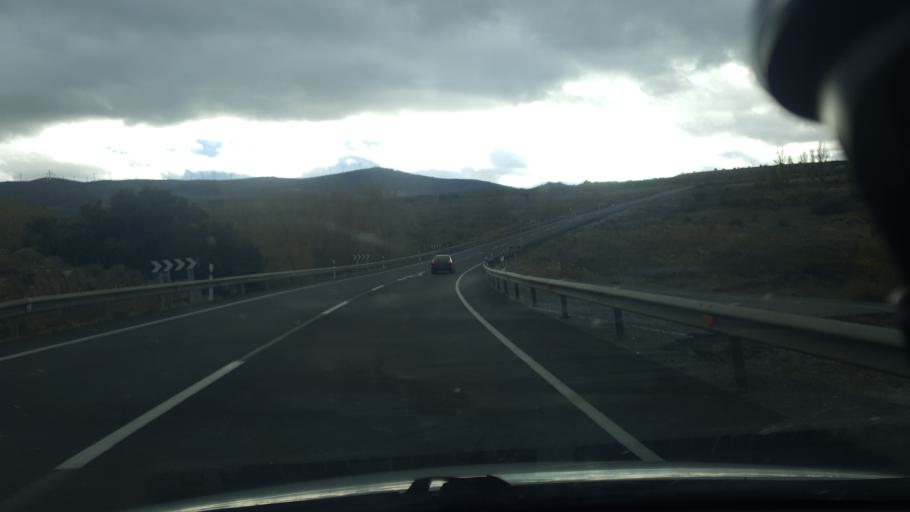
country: ES
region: Castille and Leon
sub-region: Provincia de Segovia
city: Villacastin
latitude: 40.7600
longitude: -4.4365
